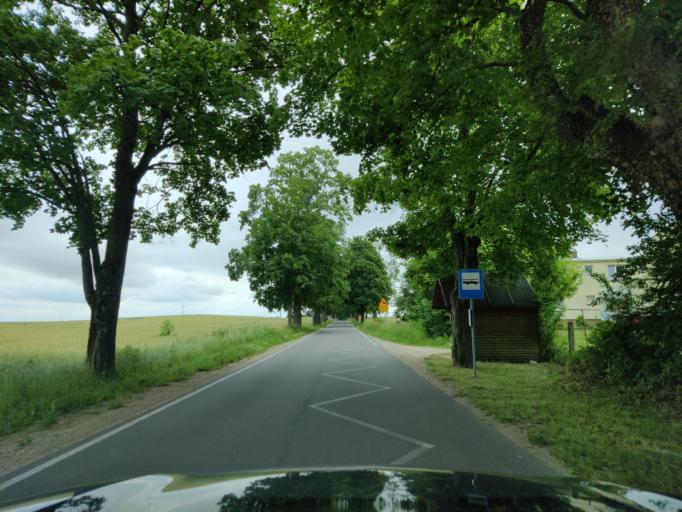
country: PL
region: Warmian-Masurian Voivodeship
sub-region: Powiat mragowski
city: Mikolajki
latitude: 53.8626
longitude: 21.6026
